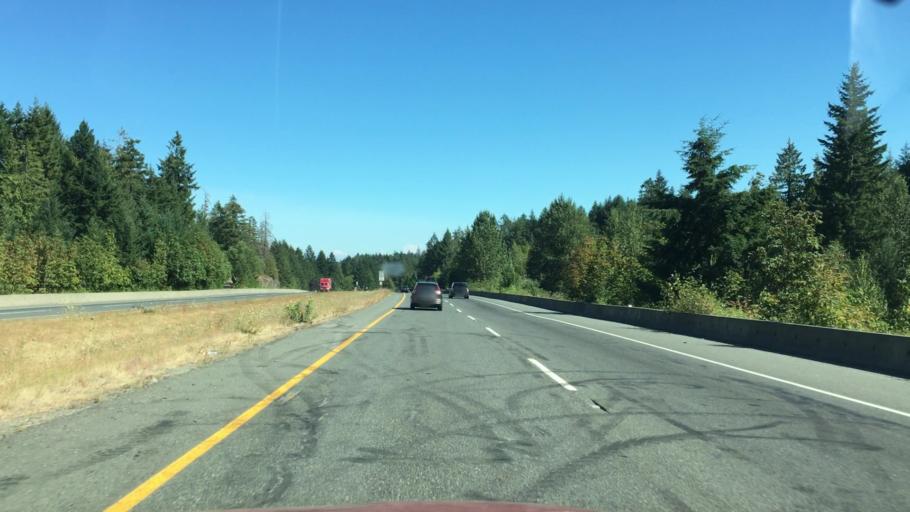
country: CA
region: British Columbia
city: Nanaimo
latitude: 49.1417
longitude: -123.9648
